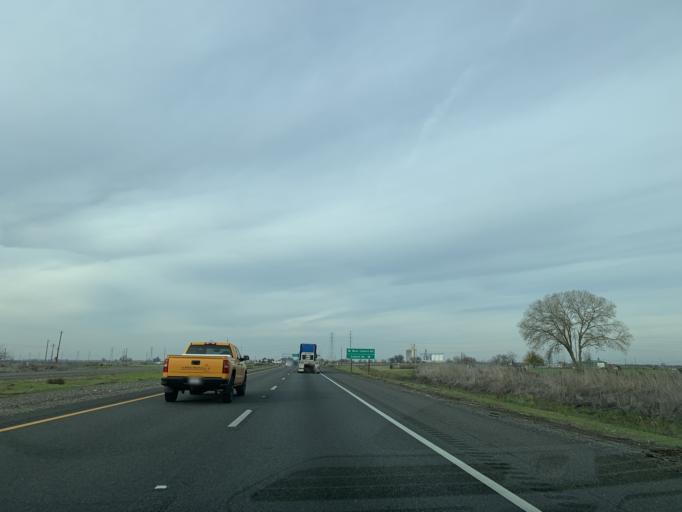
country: US
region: California
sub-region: Sacramento County
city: Elverta
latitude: 38.8340
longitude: -121.5436
